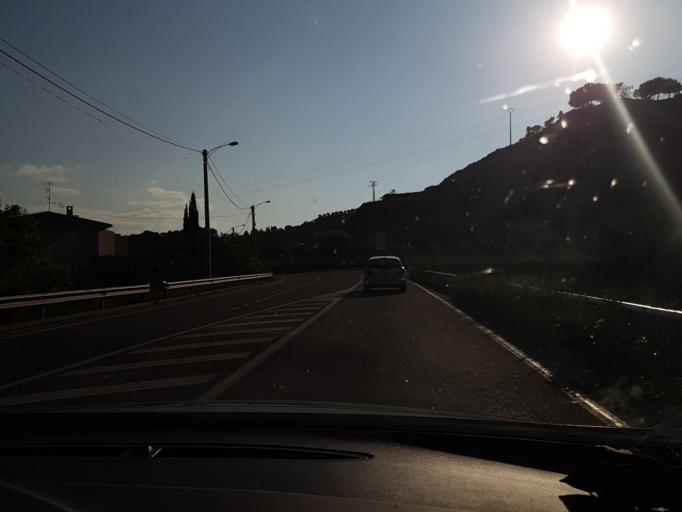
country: ES
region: La Rioja
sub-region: Provincia de La Rioja
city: Arnedo
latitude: 42.2199
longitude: -2.1166
